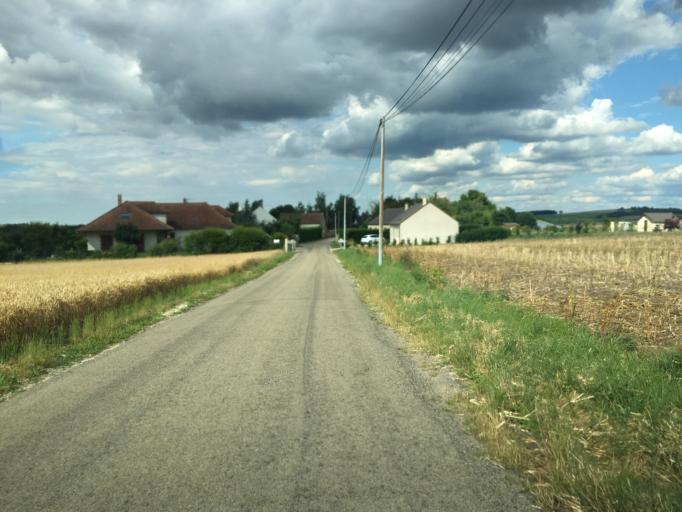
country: FR
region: Bourgogne
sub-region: Departement de l'Yonne
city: Aillant-sur-Tholon
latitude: 47.8228
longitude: 3.3927
